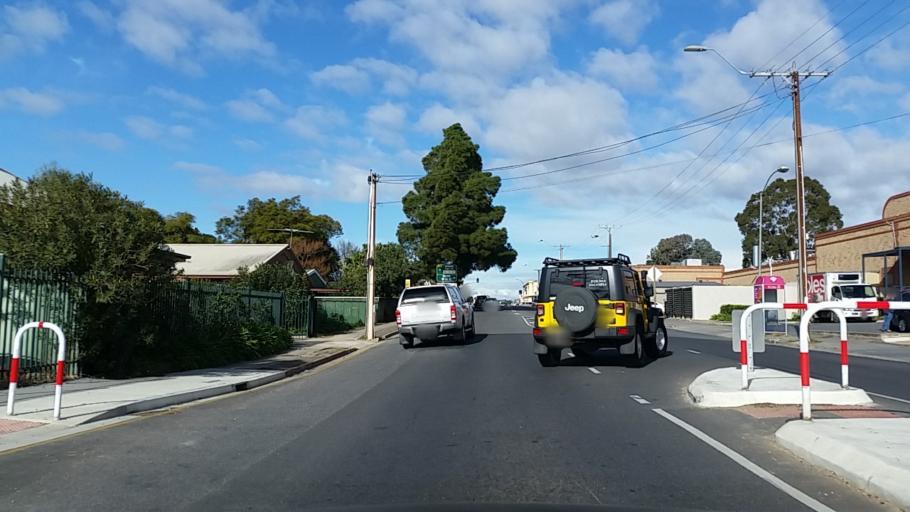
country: AU
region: South Australia
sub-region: Gawler
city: Gawler
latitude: -34.5945
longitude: 138.7490
